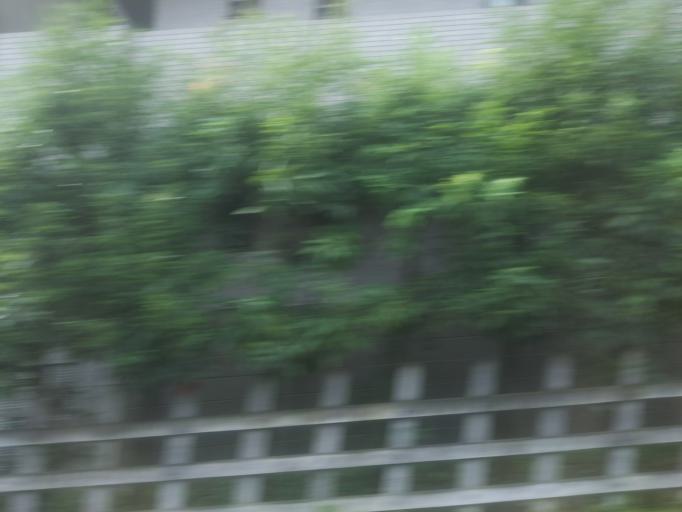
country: JP
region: Saitama
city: Wako
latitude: 35.7229
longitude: 139.6323
